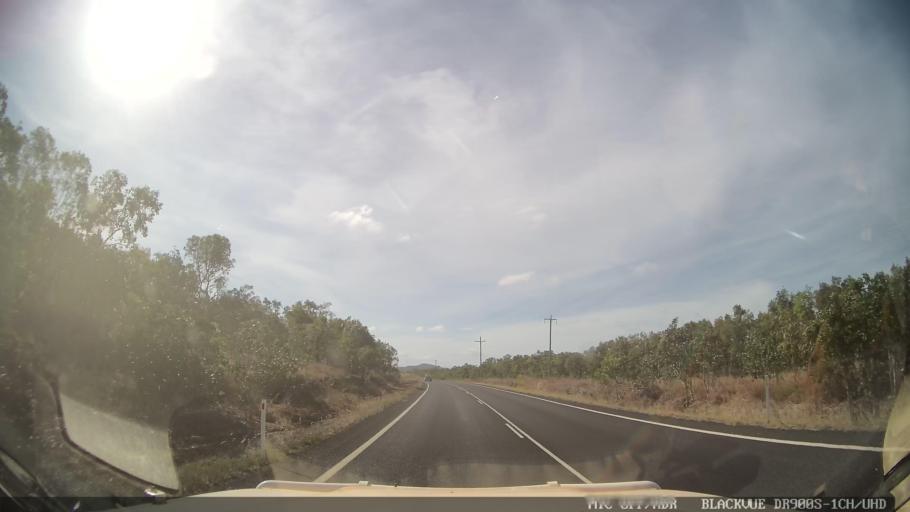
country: AU
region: Queensland
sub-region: Cook
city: Cooktown
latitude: -15.5510
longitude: 145.2422
